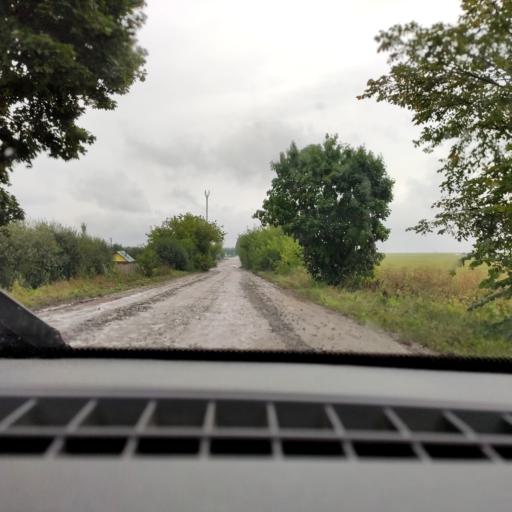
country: RU
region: Bashkortostan
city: Avdon
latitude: 54.7184
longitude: 55.7689
